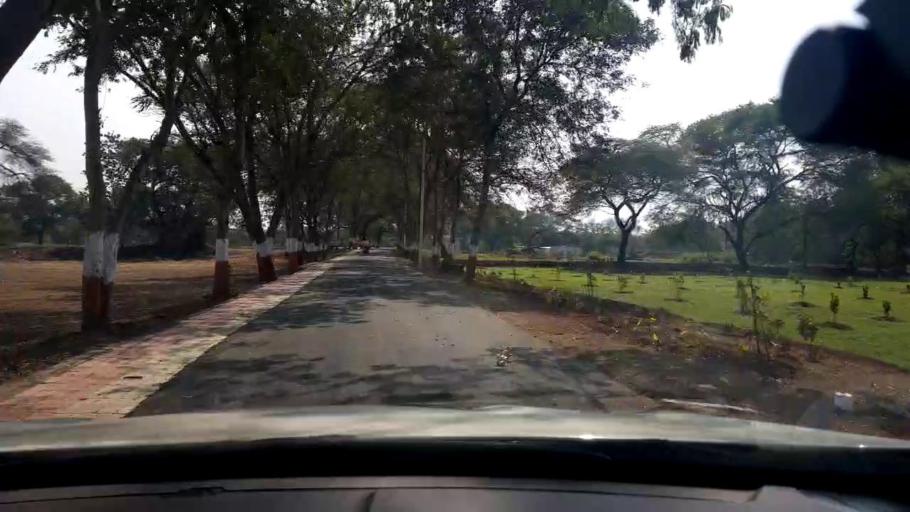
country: IN
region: Maharashtra
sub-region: Pune Division
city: Shivaji Nagar
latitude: 18.5416
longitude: 73.8557
